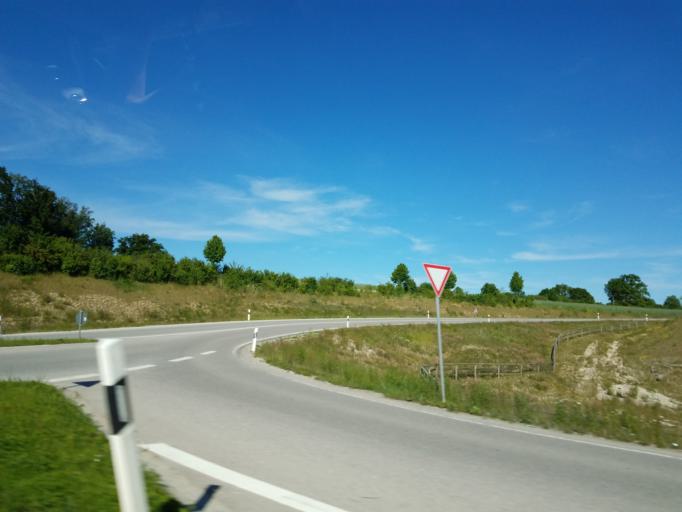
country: DE
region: Bavaria
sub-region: Upper Bavaria
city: Gilching
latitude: 48.0672
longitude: 11.3077
